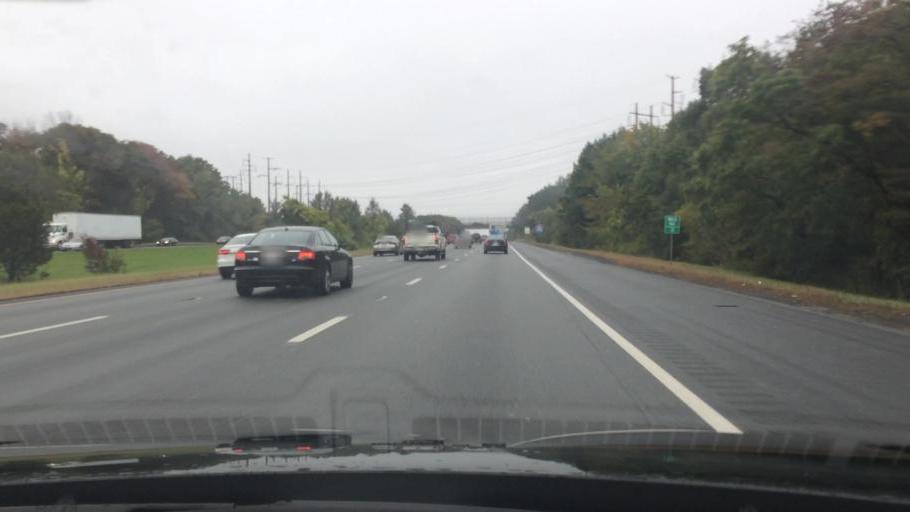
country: US
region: Massachusetts
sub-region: Middlesex County
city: Tewksbury
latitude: 42.6402
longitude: -71.2373
